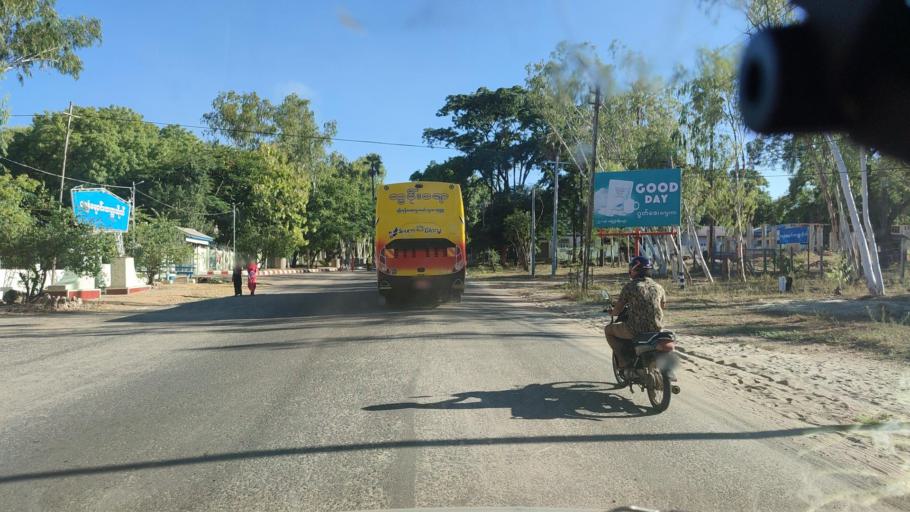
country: MM
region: Magway
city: Yenangyaung
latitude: 20.4305
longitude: 94.8801
